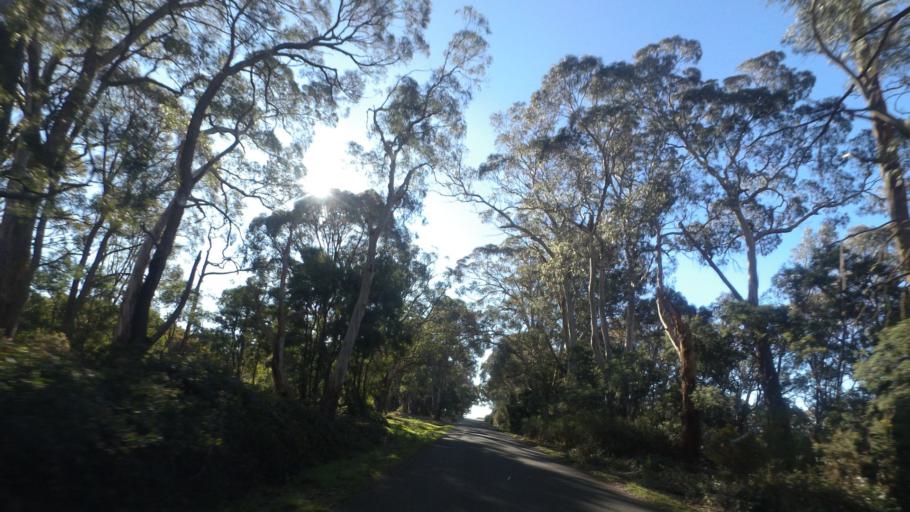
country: AU
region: Victoria
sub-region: Mount Alexander
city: Castlemaine
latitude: -37.3051
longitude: 144.3301
